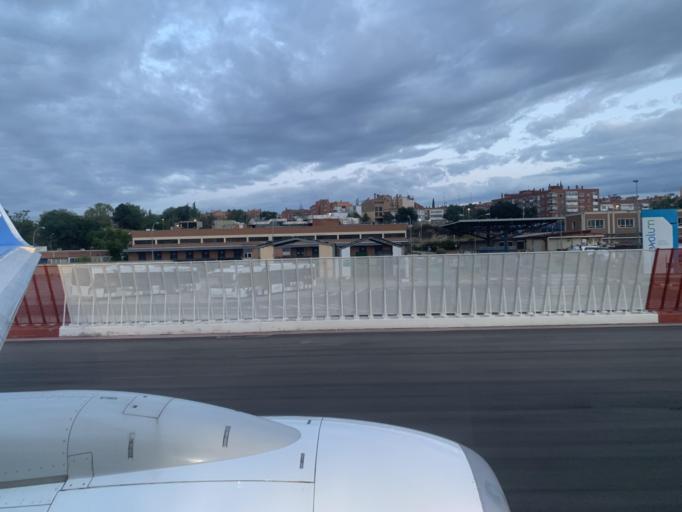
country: ES
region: Madrid
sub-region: Provincia de Madrid
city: Barajas de Madrid
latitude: 40.4721
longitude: -3.5722
